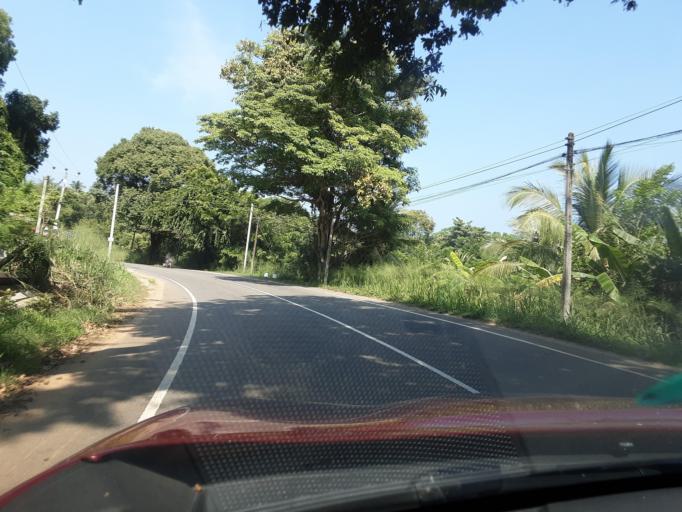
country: LK
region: Uva
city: Badulla
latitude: 7.1962
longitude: 81.0207
